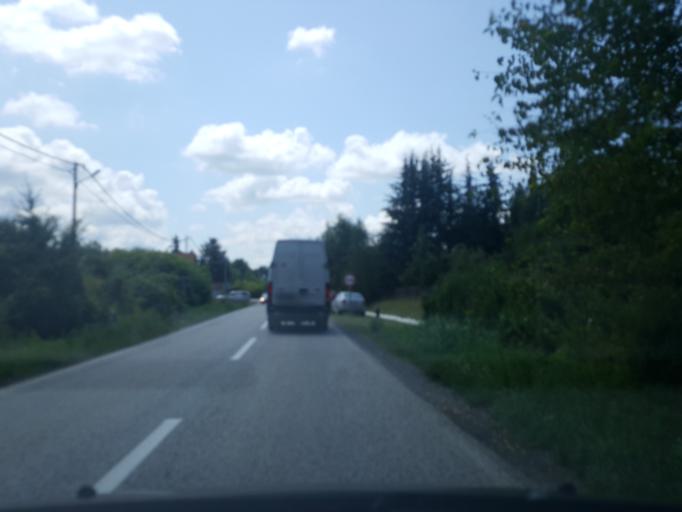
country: RS
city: Glusci
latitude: 44.8988
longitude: 19.5446
